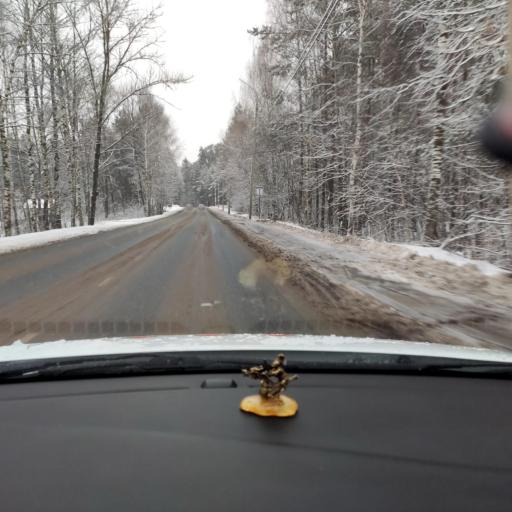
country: RU
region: Tatarstan
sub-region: Zelenodol'skiy Rayon
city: Zelenodolsk
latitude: 55.8649
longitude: 48.5370
